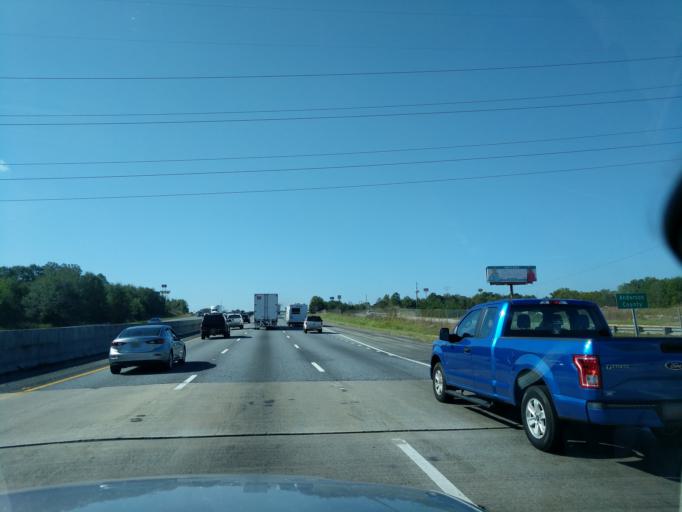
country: US
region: South Carolina
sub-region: Greenville County
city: Gantt
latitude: 34.7812
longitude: -82.4560
